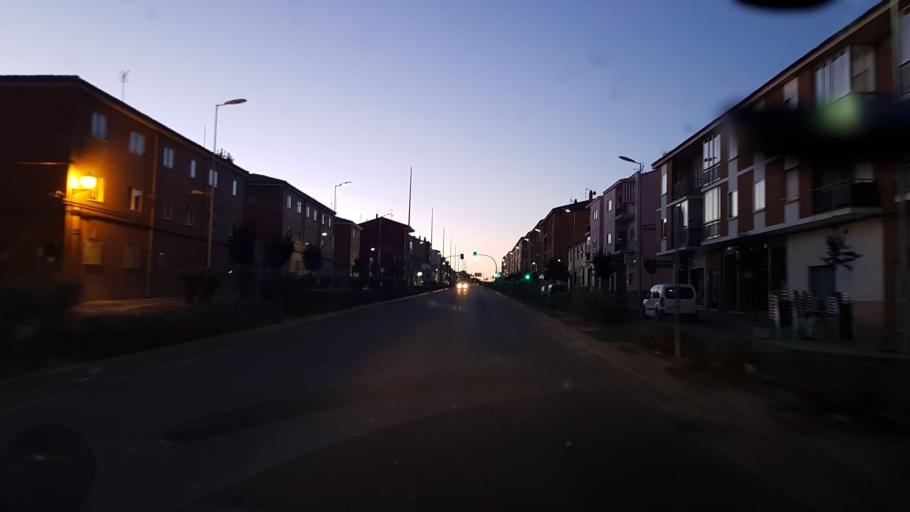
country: ES
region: Castille and Leon
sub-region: Provincia de Zamora
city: Toro
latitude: 41.5268
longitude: -5.3970
